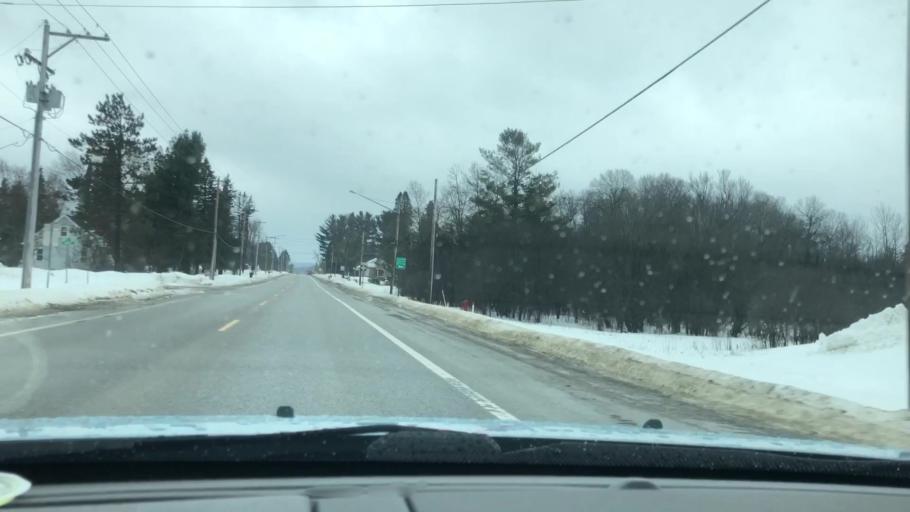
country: US
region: Michigan
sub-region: Charlevoix County
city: East Jordan
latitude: 45.1481
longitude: -85.1192
